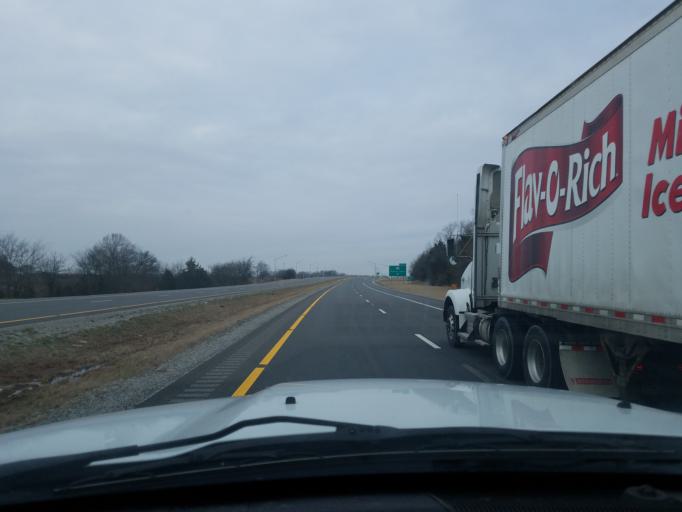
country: US
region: Kentucky
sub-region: Warren County
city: Bowling Green
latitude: 36.9397
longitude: -86.4765
